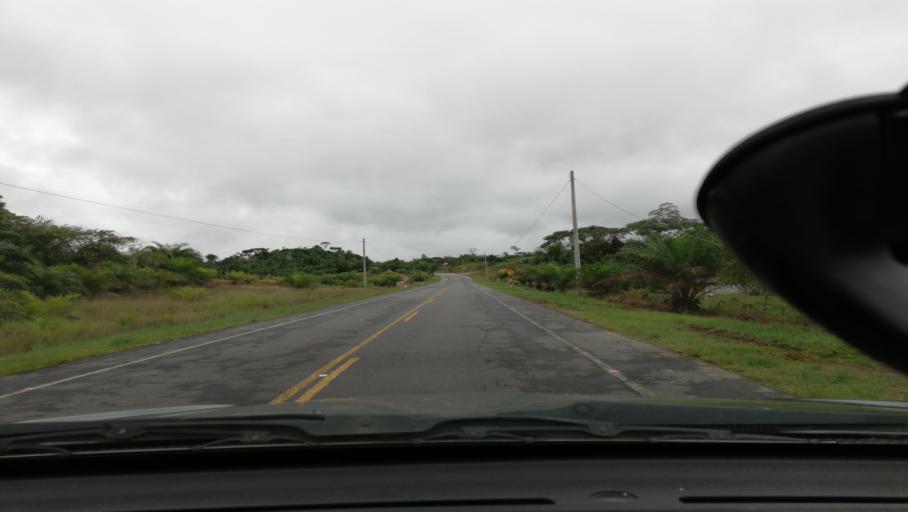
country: PE
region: Loreto
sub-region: Provincia de Loreto
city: Nauta
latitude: -4.3458
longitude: -73.5416
